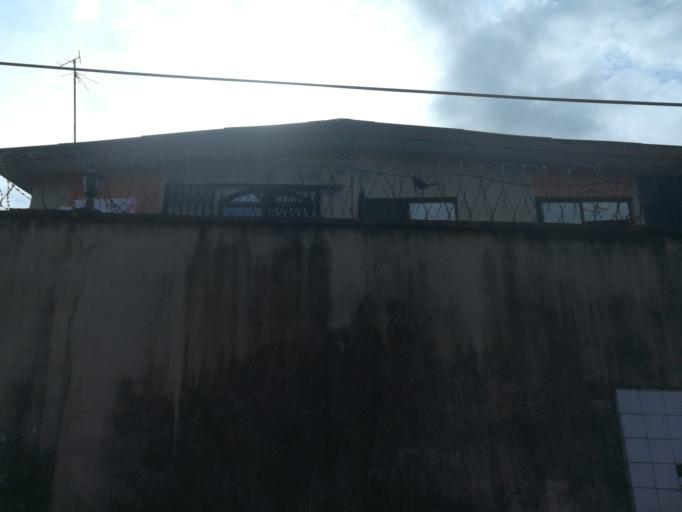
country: NG
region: Lagos
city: Somolu
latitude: 6.5422
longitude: 3.3816
